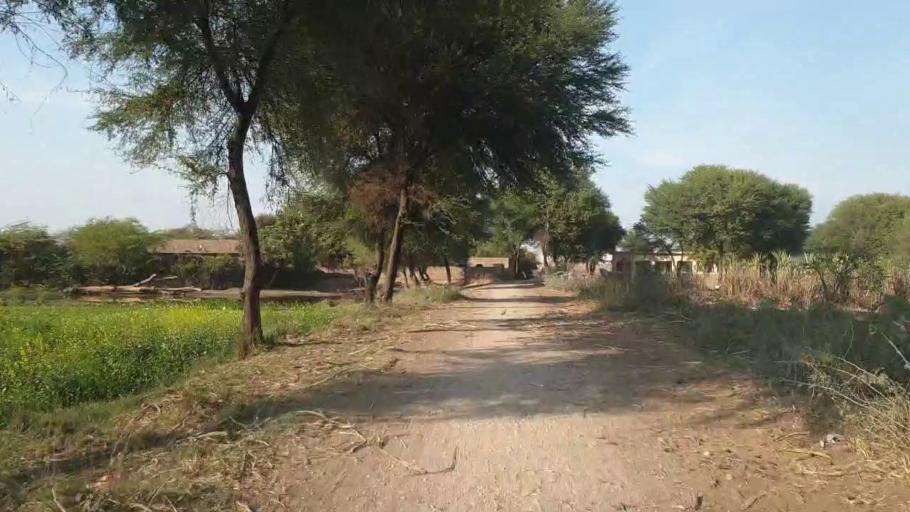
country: PK
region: Sindh
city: Chambar
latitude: 25.3186
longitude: 68.7902
